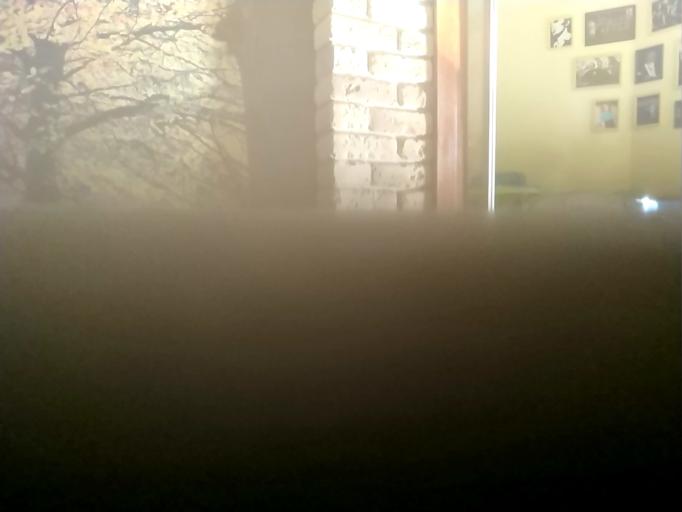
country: RU
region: Smolensk
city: Temkino
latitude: 54.9113
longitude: 34.9713
